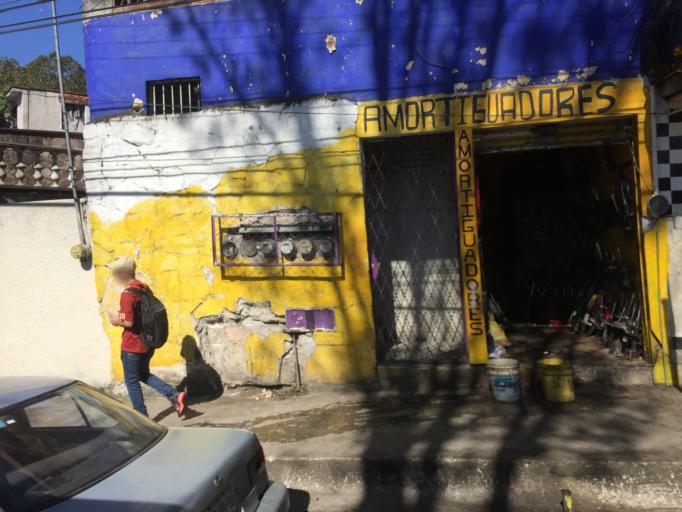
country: MX
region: Veracruz
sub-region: Xalapa
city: Xalapa de Enriquez
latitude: 19.5435
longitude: -96.9269
